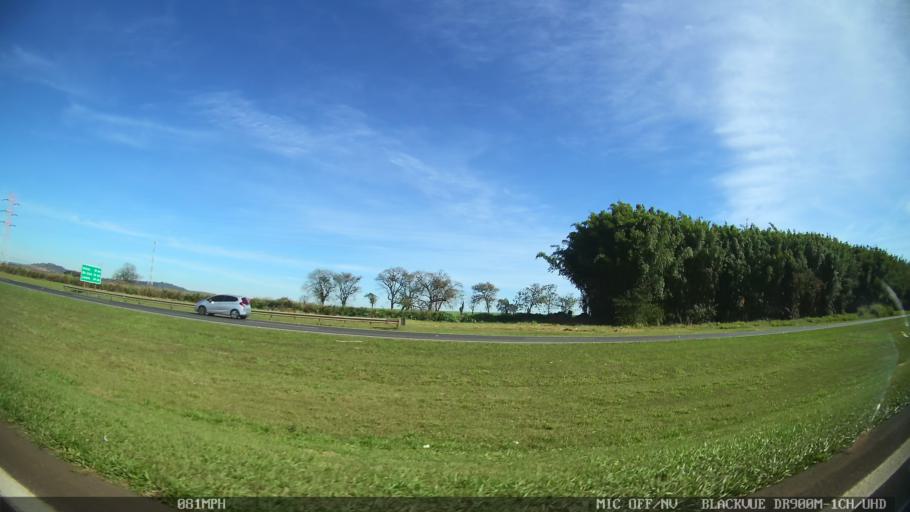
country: BR
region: Sao Paulo
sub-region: Araras
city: Araras
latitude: -22.2838
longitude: -47.3934
